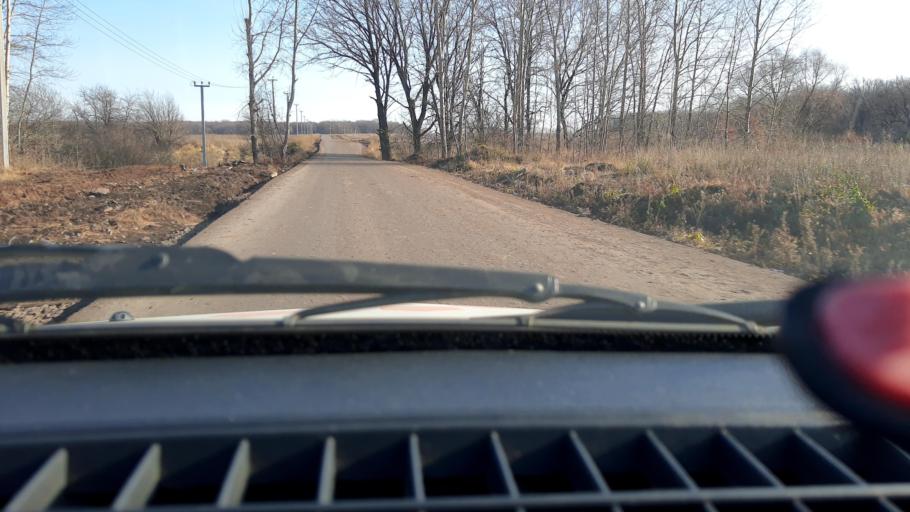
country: RU
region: Bashkortostan
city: Kabakovo
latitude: 54.6242
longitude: 56.1418
